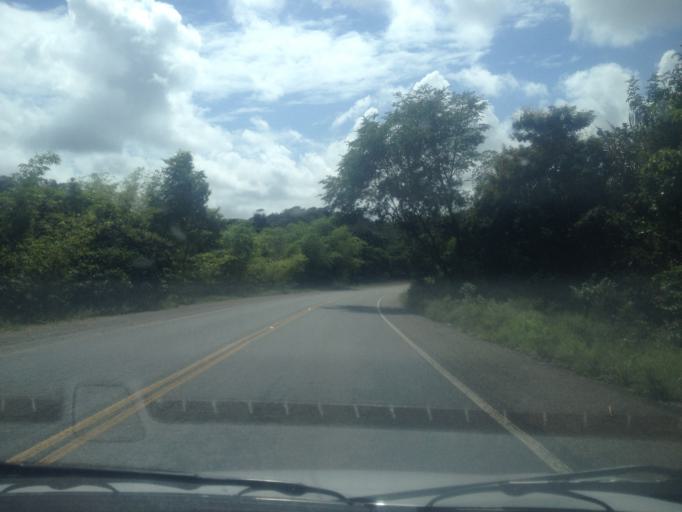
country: BR
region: Bahia
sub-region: Conde
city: Conde
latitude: -12.0405
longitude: -37.7061
